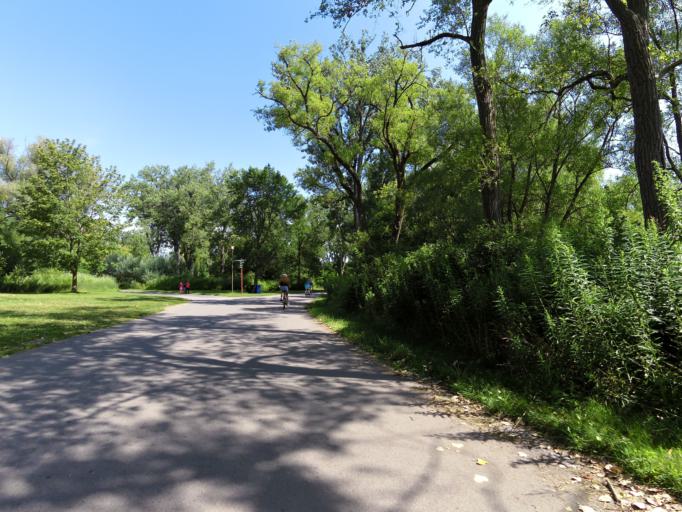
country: CA
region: Ontario
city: Toronto
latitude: 43.6148
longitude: -79.3898
